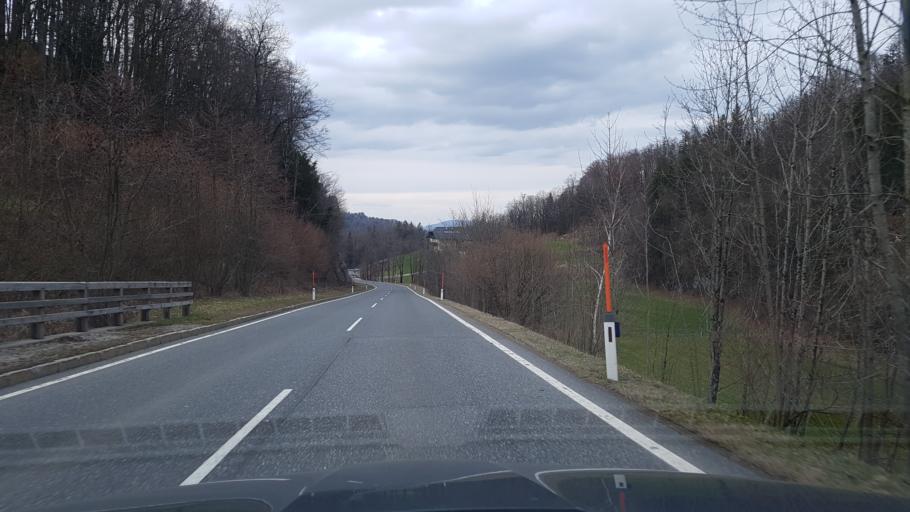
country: AT
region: Salzburg
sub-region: Politischer Bezirk Hallein
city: Hallein
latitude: 47.6648
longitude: 13.0945
